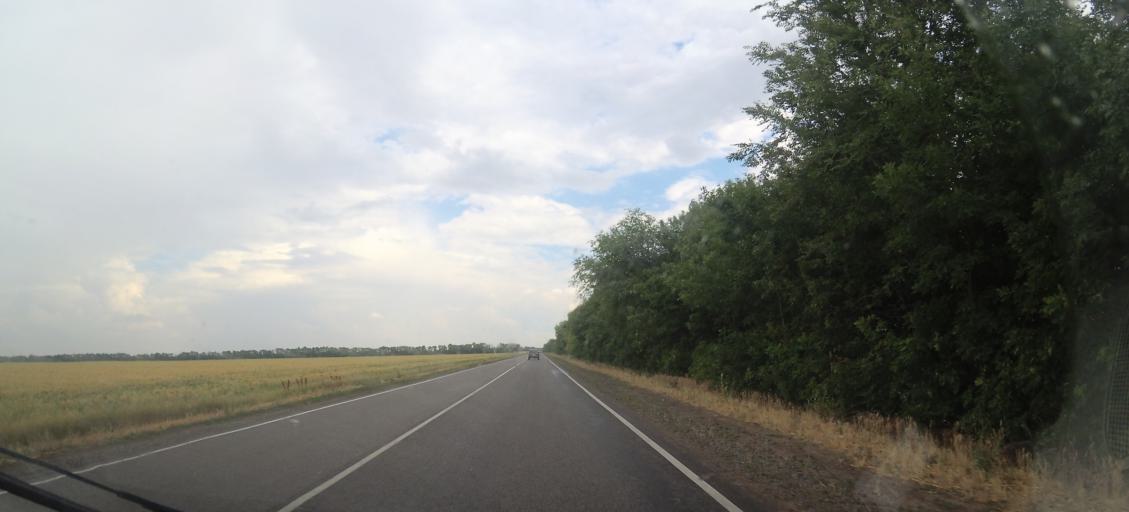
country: RU
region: Rostov
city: Peschanokopskoye
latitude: 46.1998
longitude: 41.1595
